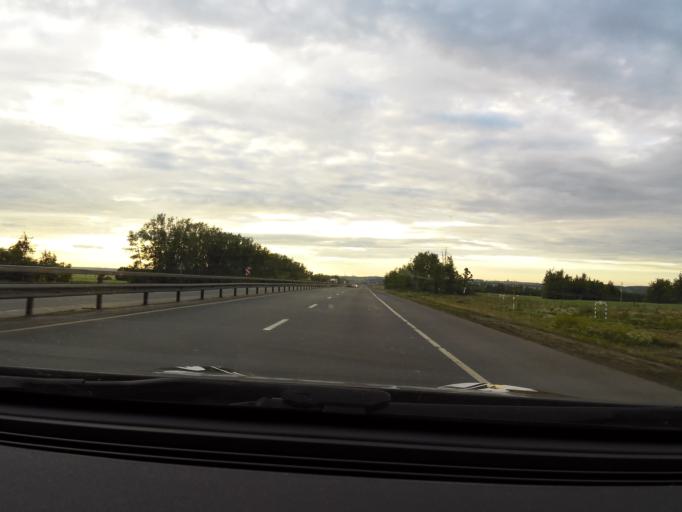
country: RU
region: Chuvashia
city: Kugesi
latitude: 55.9477
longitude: 47.3766
